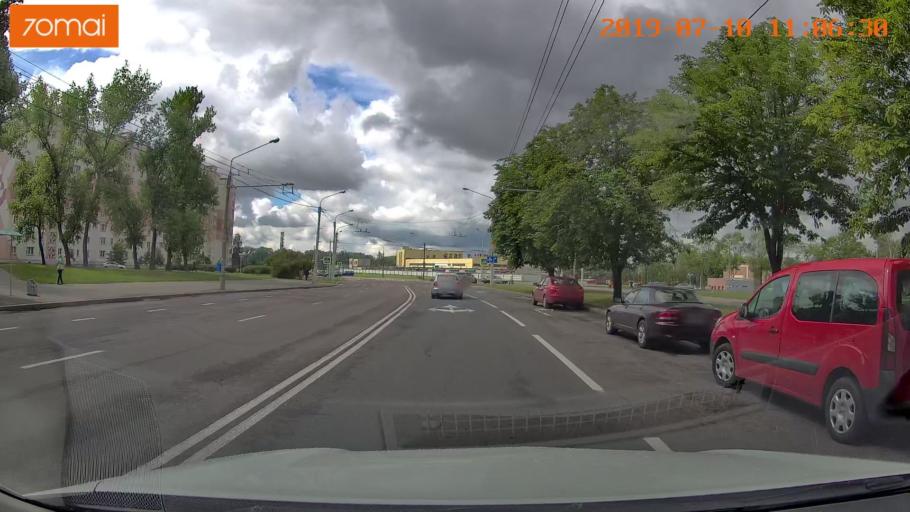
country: BY
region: Minsk
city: Syenitsa
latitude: 53.8486
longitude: 27.5447
